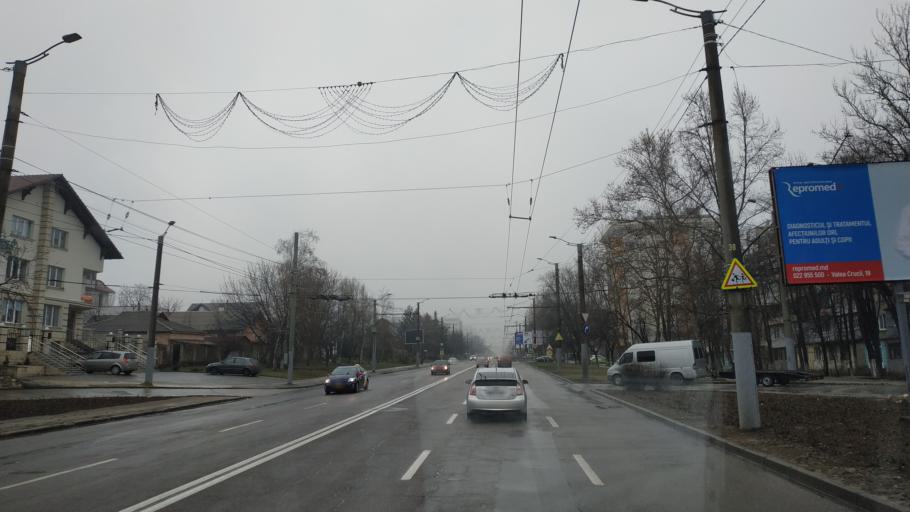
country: MD
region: Chisinau
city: Vatra
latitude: 47.0300
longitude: 28.7869
